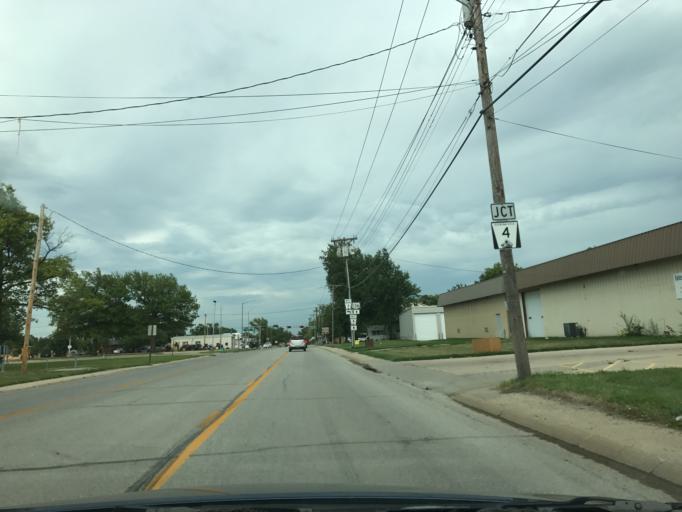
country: US
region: Nebraska
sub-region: Gage County
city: Beatrice
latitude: 40.2657
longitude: -96.7774
